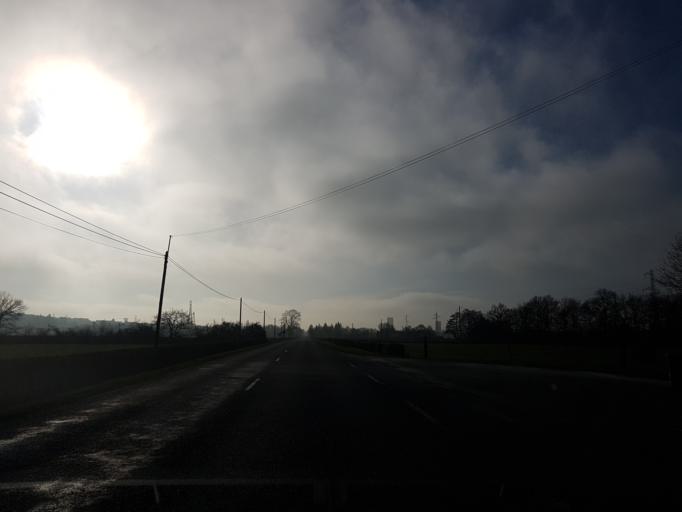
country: FR
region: Bourgogne
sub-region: Departement de Saone-et-Loire
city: Gueugnon
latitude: 46.6172
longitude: 4.0799
